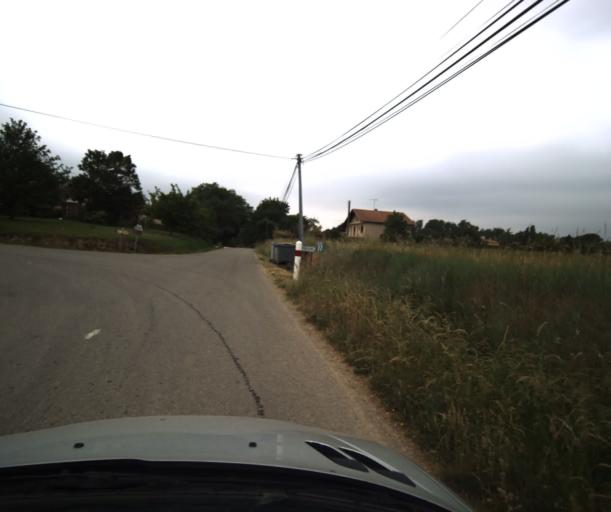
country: FR
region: Midi-Pyrenees
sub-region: Departement du Tarn-et-Garonne
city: Saint-Nicolas-de-la-Grave
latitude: 44.0593
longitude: 0.9748
